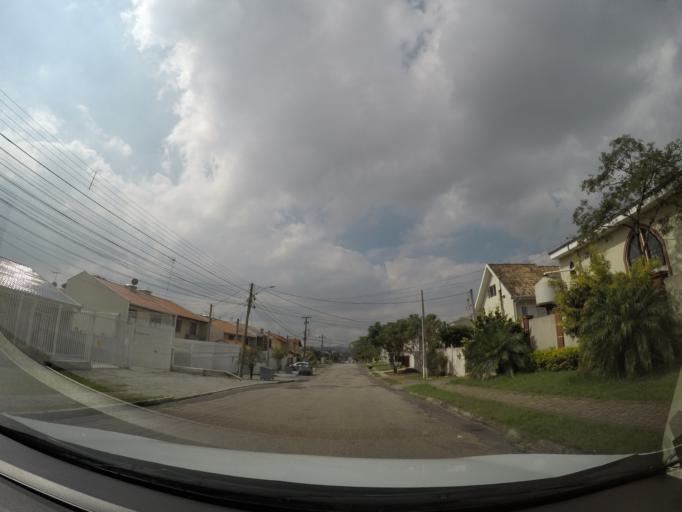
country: BR
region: Parana
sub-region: Sao Jose Dos Pinhais
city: Sao Jose dos Pinhais
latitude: -25.4975
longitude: -49.2503
